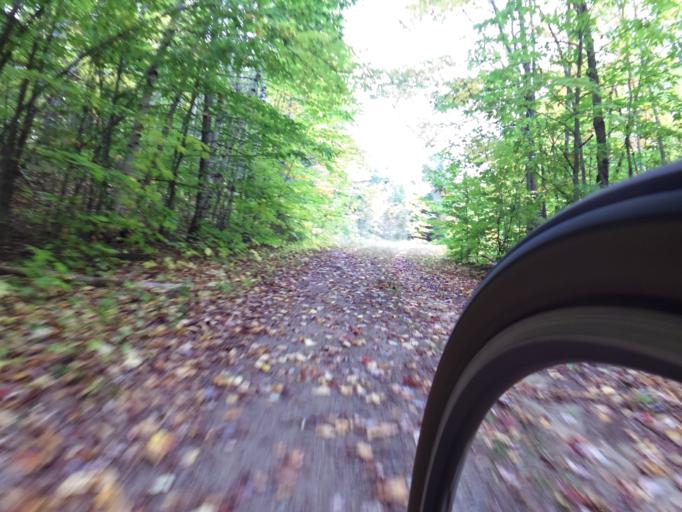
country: CA
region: Quebec
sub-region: Outaouais
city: Wakefield
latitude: 45.5980
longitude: -76.0687
